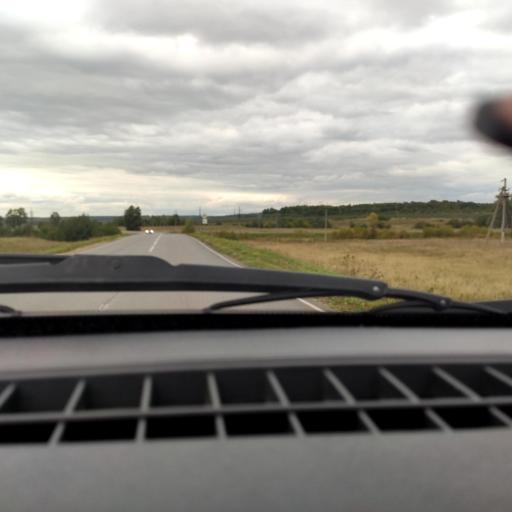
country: RU
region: Bashkortostan
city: Iglino
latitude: 54.7255
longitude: 56.4054
